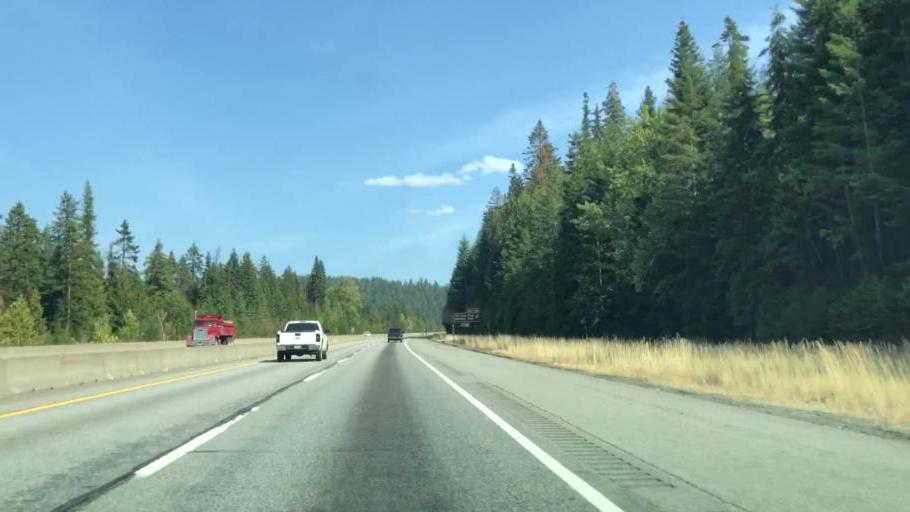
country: US
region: Idaho
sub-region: Kootenai County
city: Coeur d'Alene
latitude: 47.6246
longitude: -116.5426
